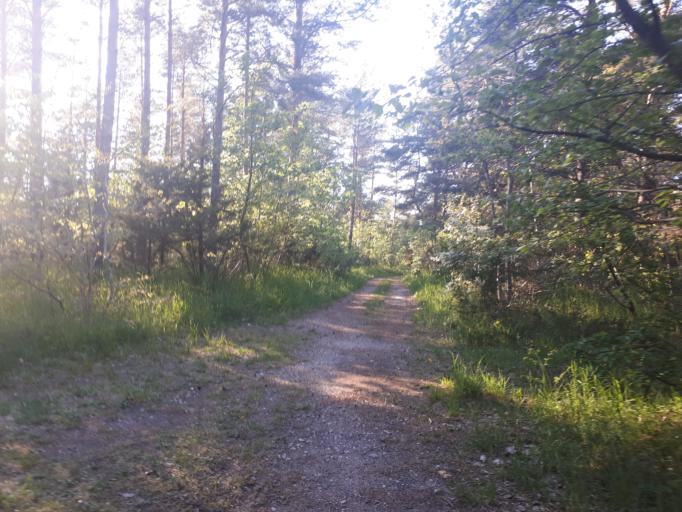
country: SE
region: Gotland
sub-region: Gotland
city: Visby
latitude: 57.6087
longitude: 18.2948
